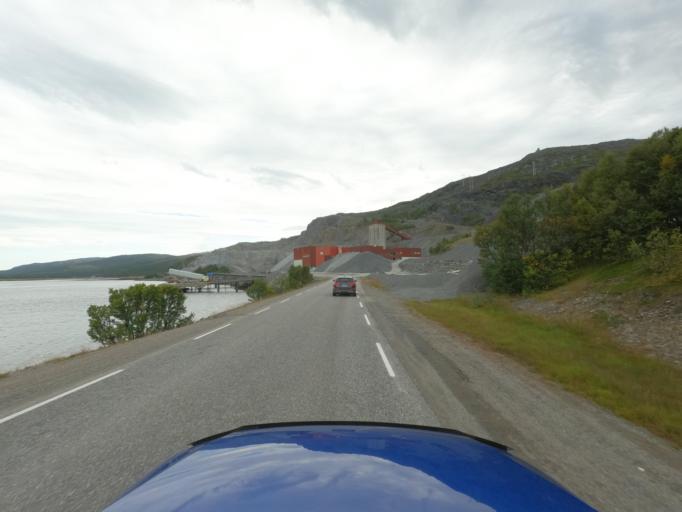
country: NO
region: Finnmark Fylke
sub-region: Kvalsund
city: Kvalsund
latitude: 70.4559
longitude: 24.2780
